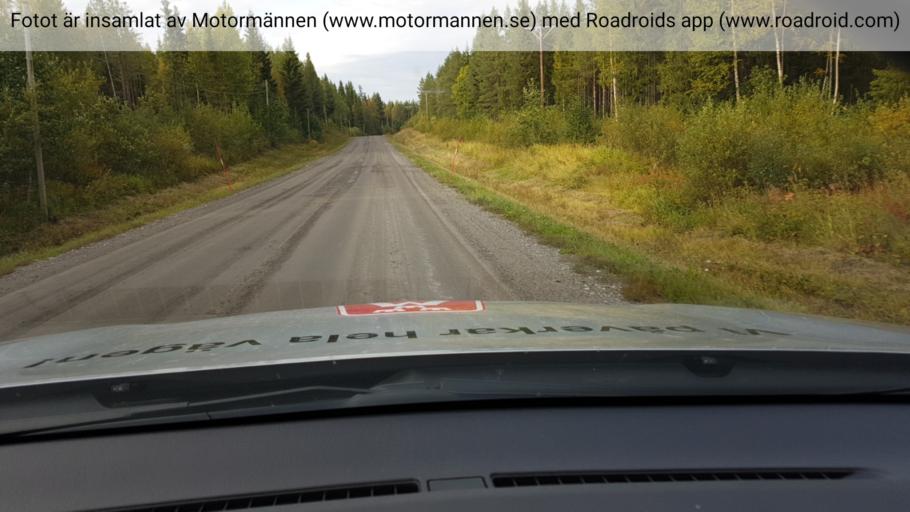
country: SE
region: Jaemtland
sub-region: Stroemsunds Kommun
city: Stroemsund
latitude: 63.9738
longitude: 15.8242
